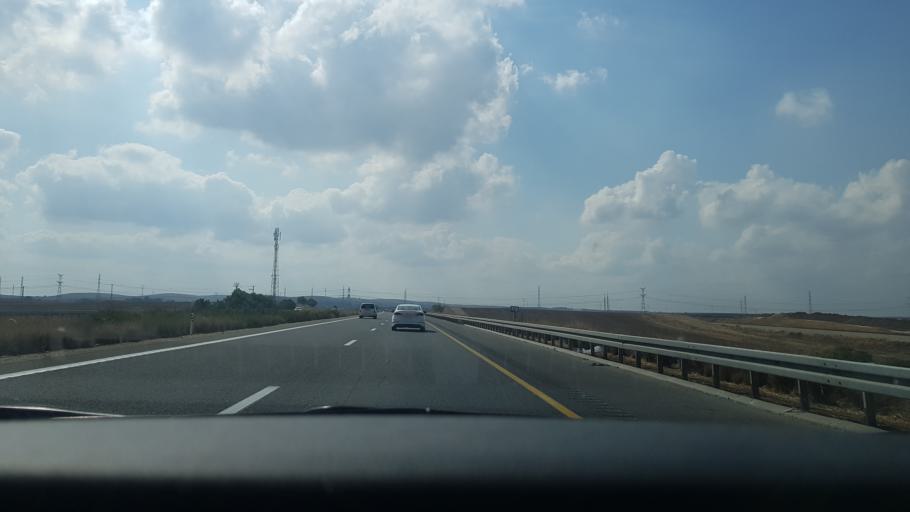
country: IL
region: Central District
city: Bene 'Ayish
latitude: 31.7217
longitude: 34.8204
